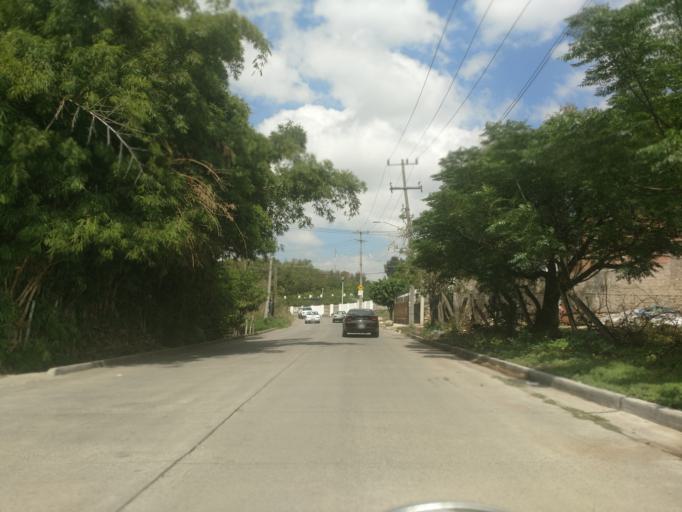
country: MX
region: Jalisco
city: Tlaquepaque
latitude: 20.6446
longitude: -103.2775
